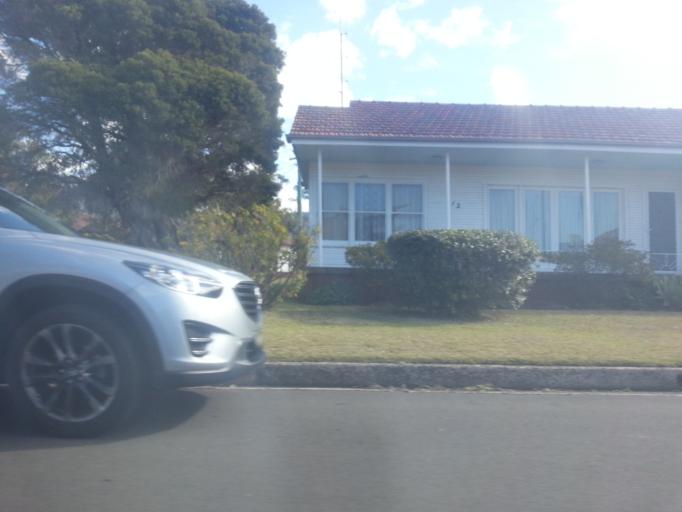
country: AU
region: New South Wales
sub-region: Wollongong
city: Fairy Meadow
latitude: -34.3944
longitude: 150.8917
